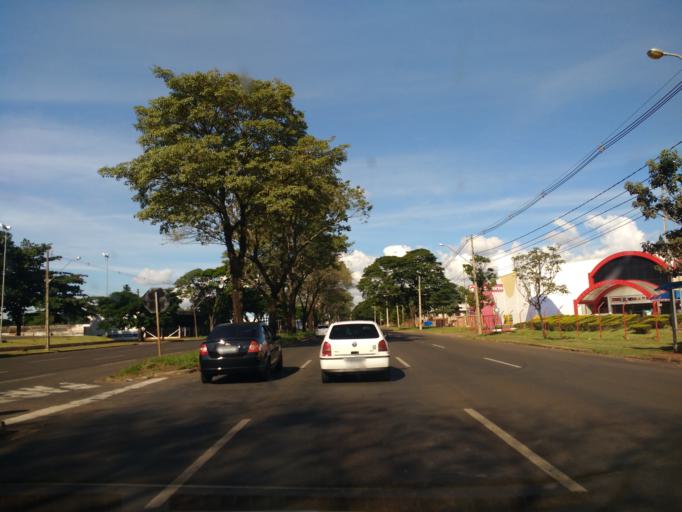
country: BR
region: Parana
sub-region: Maringa
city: Maringa
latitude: -23.4182
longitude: -51.9162
